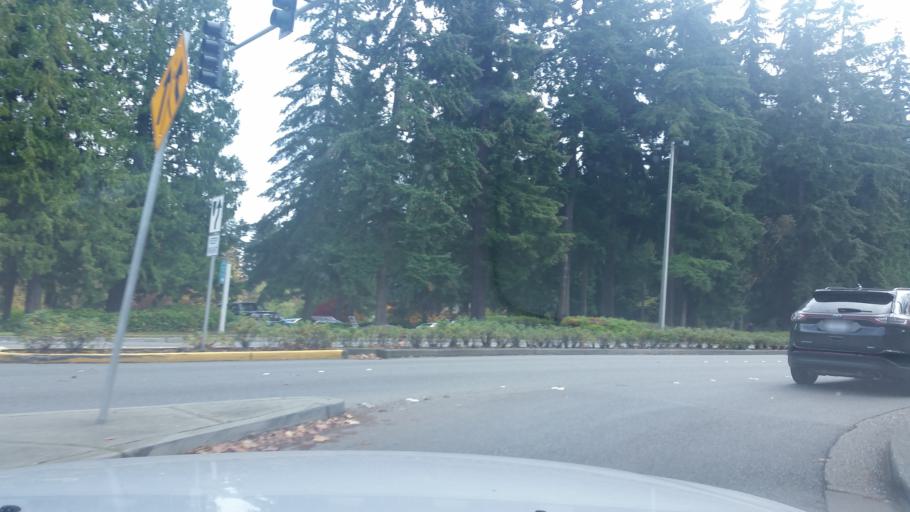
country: US
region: Washington
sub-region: King County
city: Eastgate
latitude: 47.5890
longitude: -122.1430
